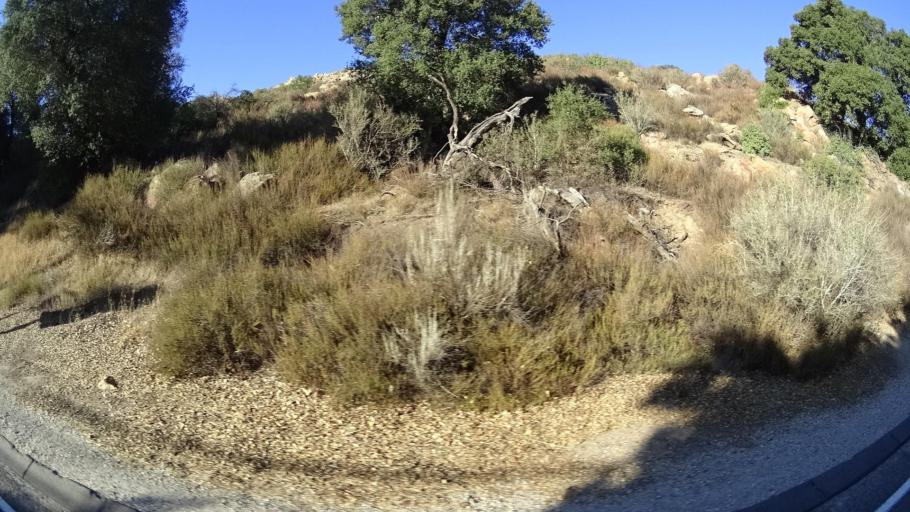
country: US
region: California
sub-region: San Diego County
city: Campo
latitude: 32.6114
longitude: -116.4747
